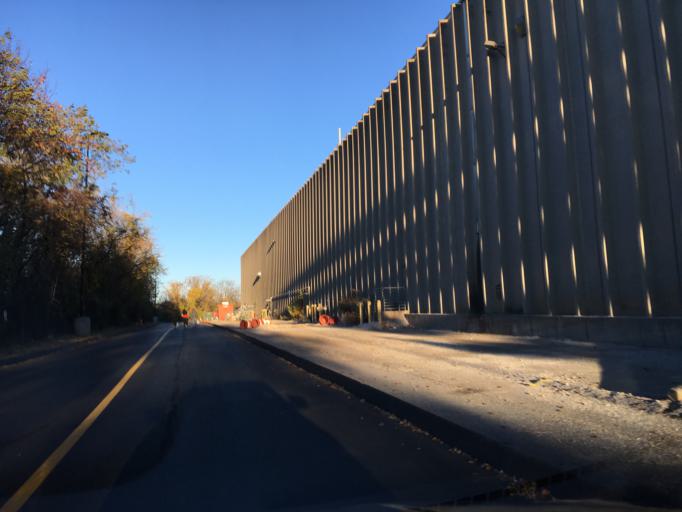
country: US
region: Maryland
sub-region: Baltimore County
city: Garrison
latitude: 39.4085
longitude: -76.7698
